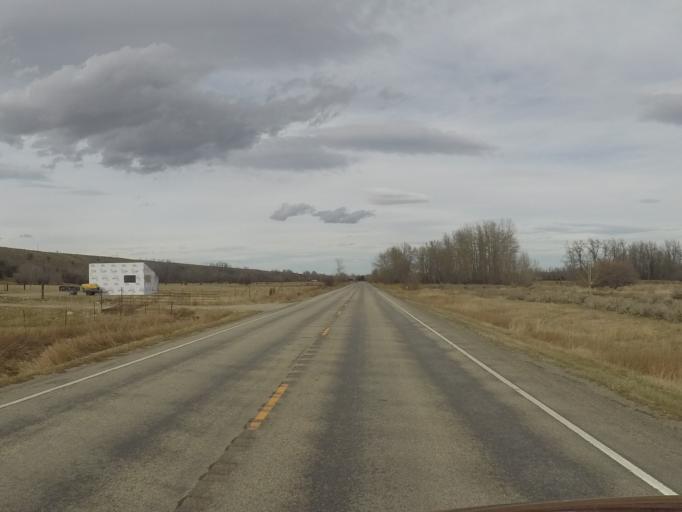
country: US
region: Montana
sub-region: Carbon County
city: Red Lodge
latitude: 45.2385
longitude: -109.2365
